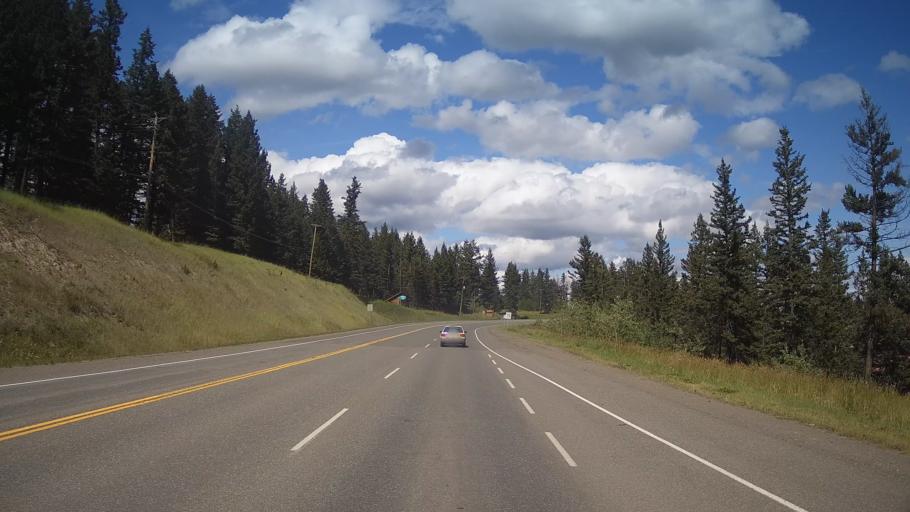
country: CA
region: British Columbia
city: Cache Creek
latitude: 51.6527
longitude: -121.2952
